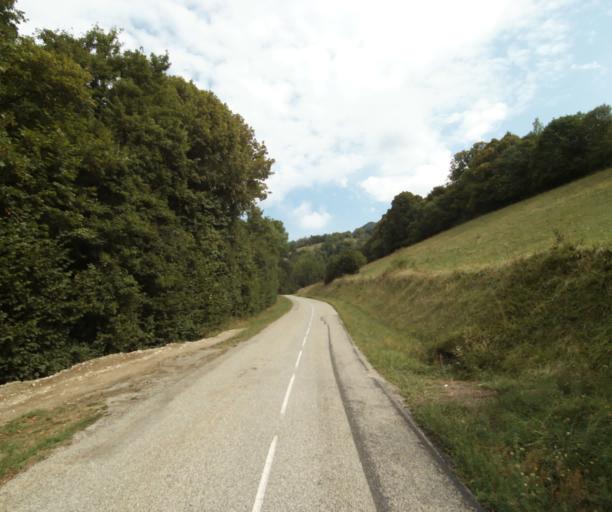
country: FR
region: Rhone-Alpes
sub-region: Departement de l'Isere
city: Saint-Egreve
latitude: 45.2717
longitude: 5.7071
